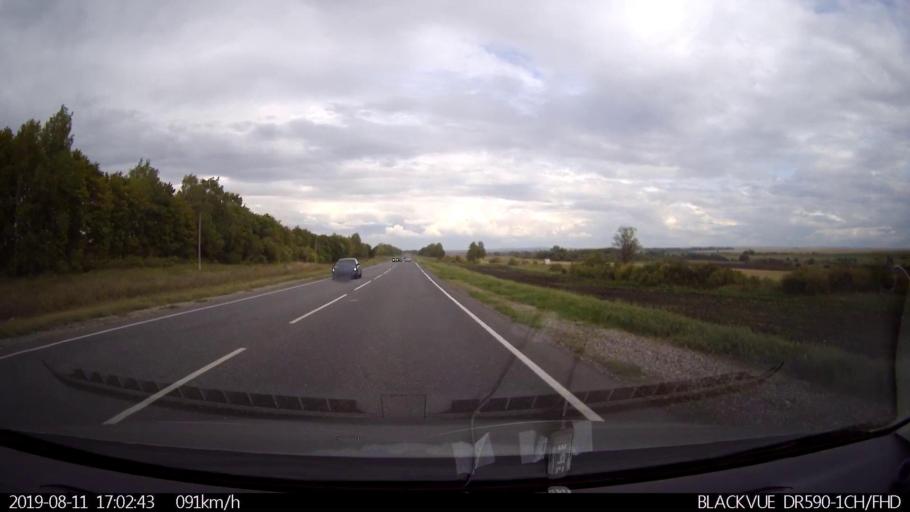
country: RU
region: Ulyanovsk
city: Mayna
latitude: 54.3053
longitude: 47.7211
